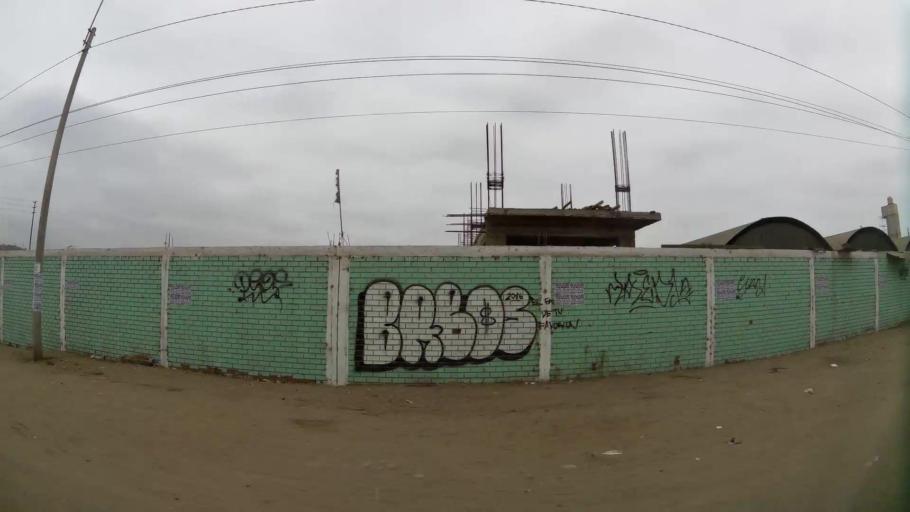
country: PE
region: Lima
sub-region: Lima
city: Surco
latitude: -12.1996
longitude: -76.9653
